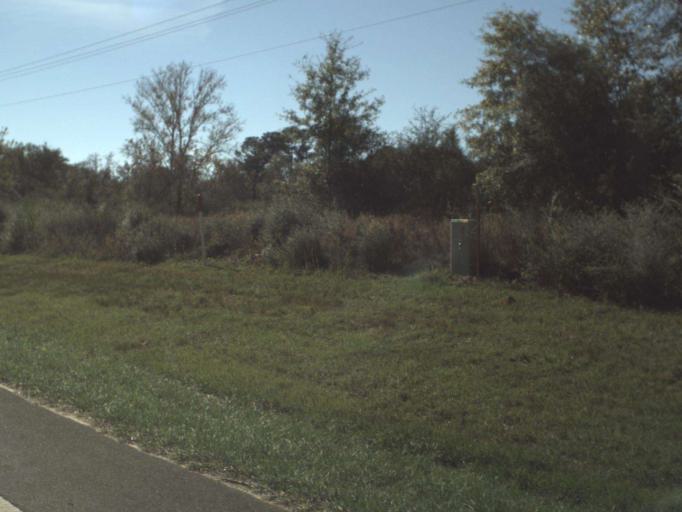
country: US
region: Florida
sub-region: Okaloosa County
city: Crestview
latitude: 30.8161
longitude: -86.6776
